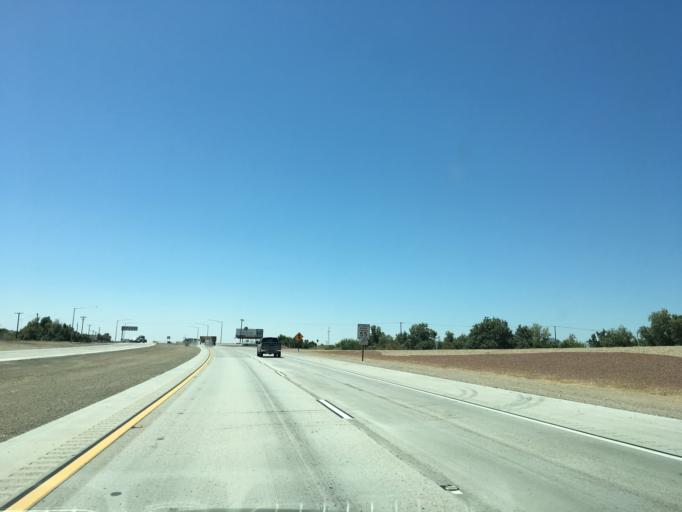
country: US
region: Arizona
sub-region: Yuma County
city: Yuma
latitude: 32.7319
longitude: -114.6247
